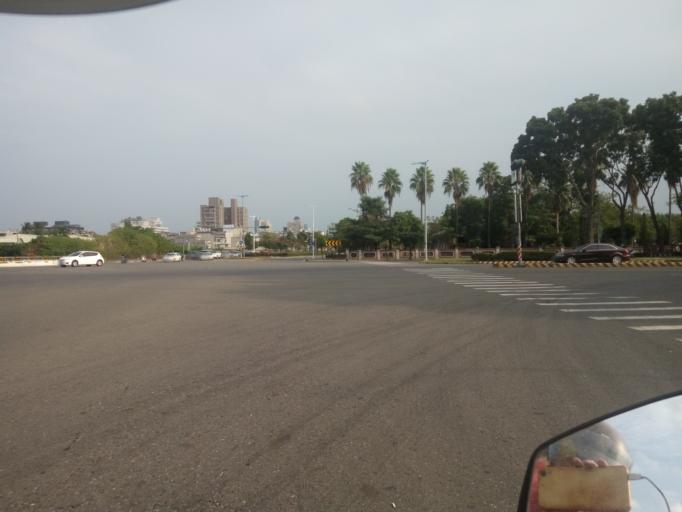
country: TW
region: Taiwan
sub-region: Chiayi
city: Jiayi Shi
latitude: 23.4817
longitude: 120.4205
